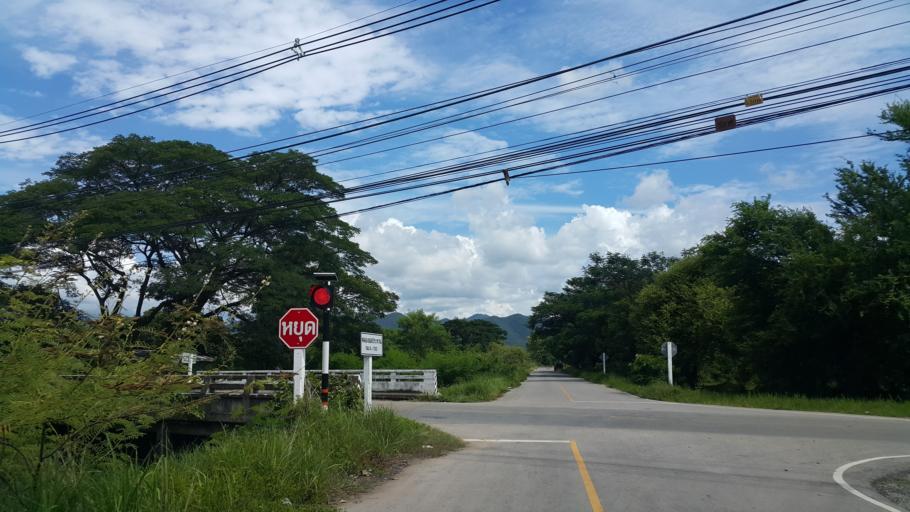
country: TH
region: Chiang Mai
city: Mae On
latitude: 18.7434
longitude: 99.2008
